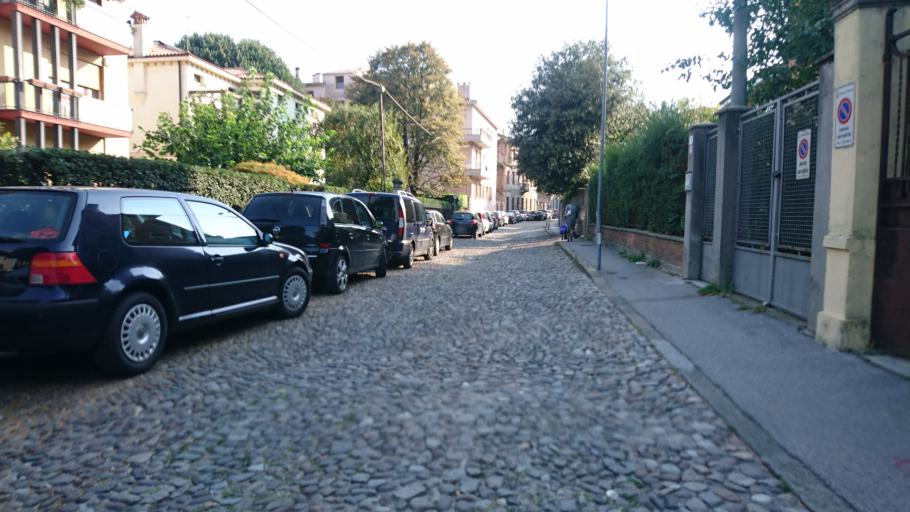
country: IT
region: Veneto
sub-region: Provincia di Padova
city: Padova
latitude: 45.4136
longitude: 11.8671
